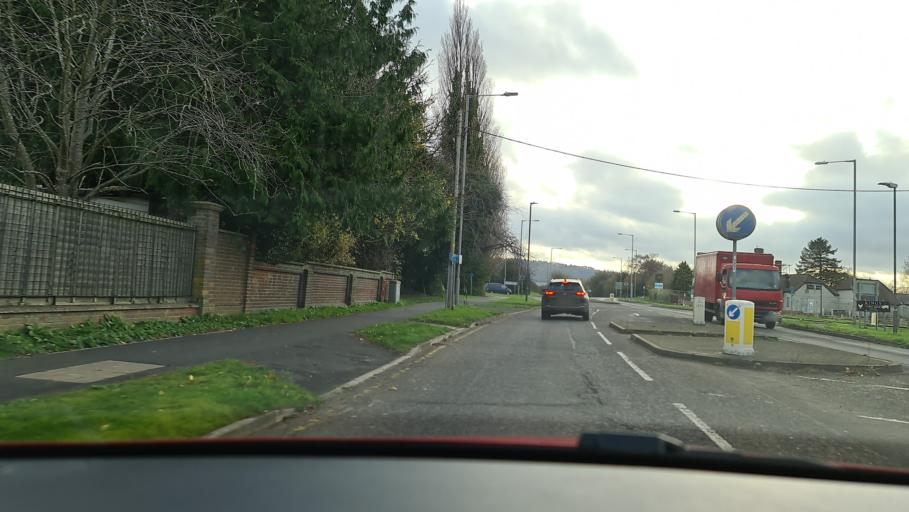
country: GB
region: England
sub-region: Buckinghamshire
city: Weston Turville
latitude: 51.7753
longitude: -0.7564
